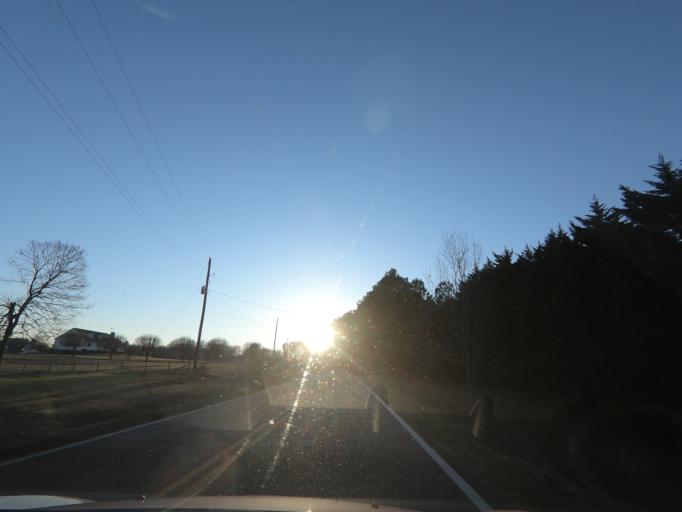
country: US
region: Georgia
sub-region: Dawson County
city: Dawsonville
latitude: 34.3307
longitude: -84.1251
